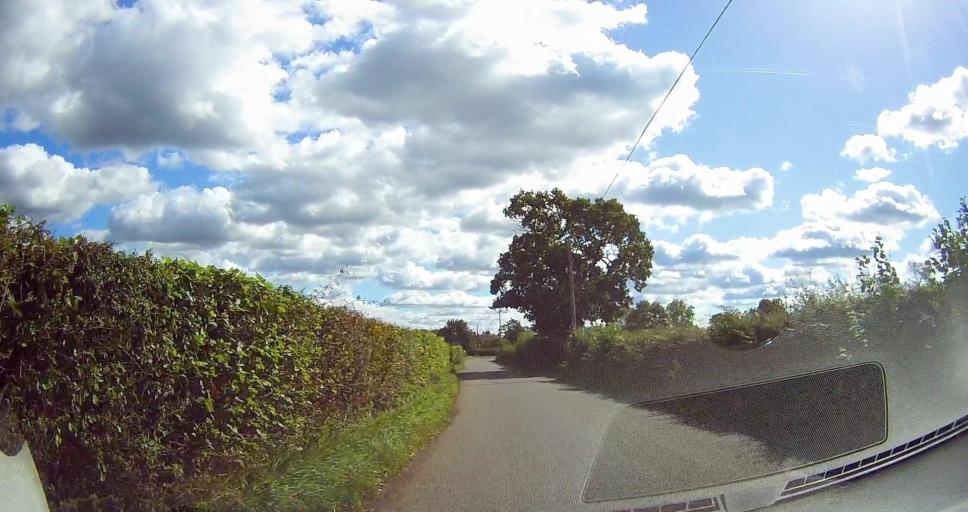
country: GB
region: England
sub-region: Cheshire East
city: Nantwich
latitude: 52.9852
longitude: -2.5321
